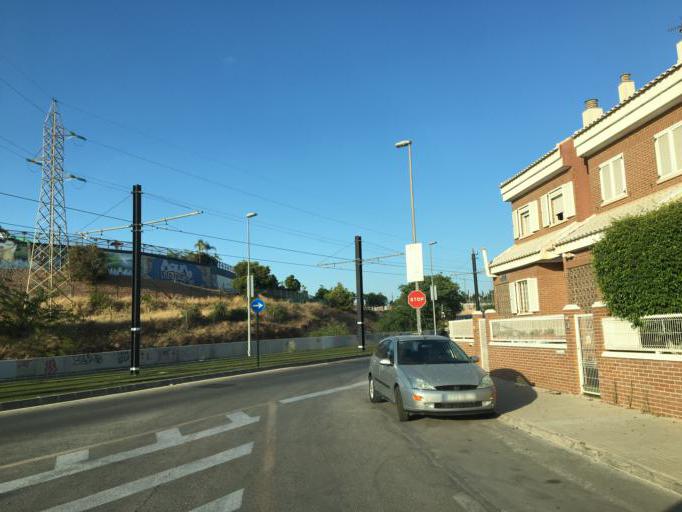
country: ES
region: Murcia
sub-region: Murcia
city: Murcia
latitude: 38.0128
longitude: -1.1630
